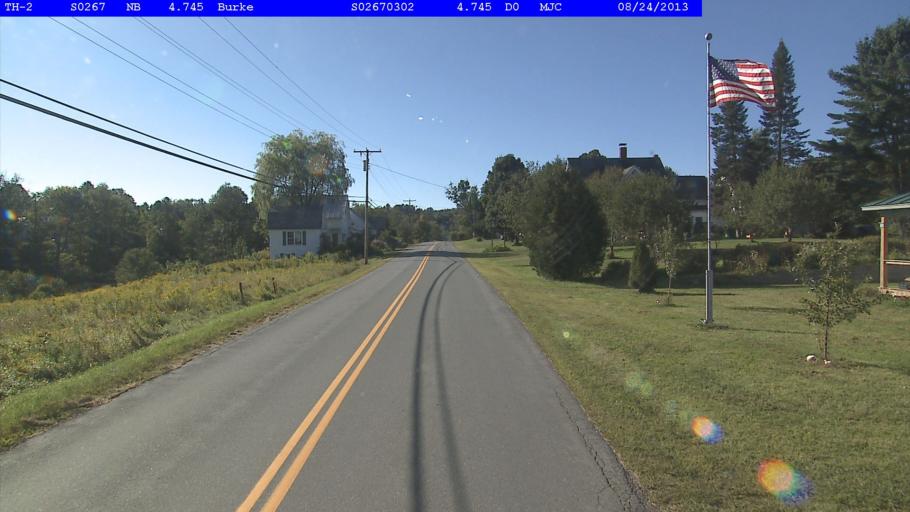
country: US
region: Vermont
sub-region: Caledonia County
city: Lyndonville
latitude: 44.6407
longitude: -71.9763
